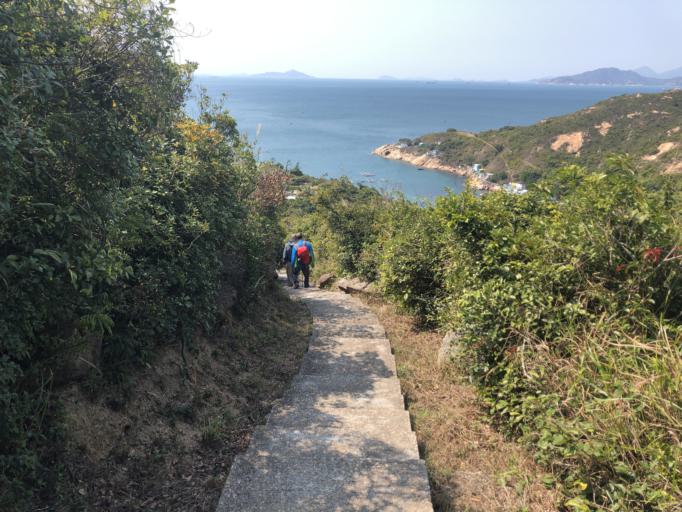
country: HK
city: Sok Kwu Wan
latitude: 22.1648
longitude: 114.2571
